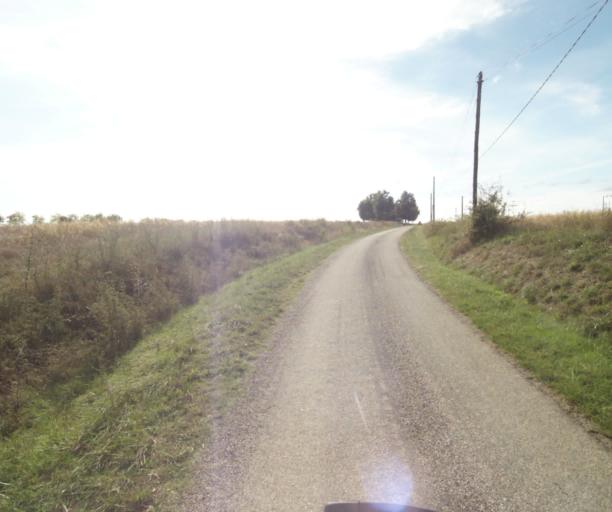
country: FR
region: Midi-Pyrenees
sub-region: Departement du Tarn-et-Garonne
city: Saint-Porquier
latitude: 43.9486
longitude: 1.1475
